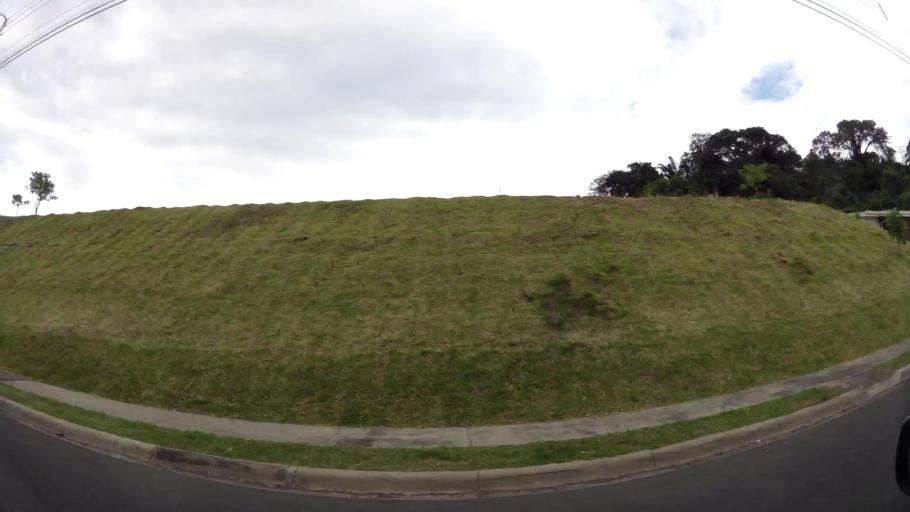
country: CR
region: Heredia
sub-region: Canton de Belen
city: San Antonio
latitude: 9.9664
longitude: -84.1876
